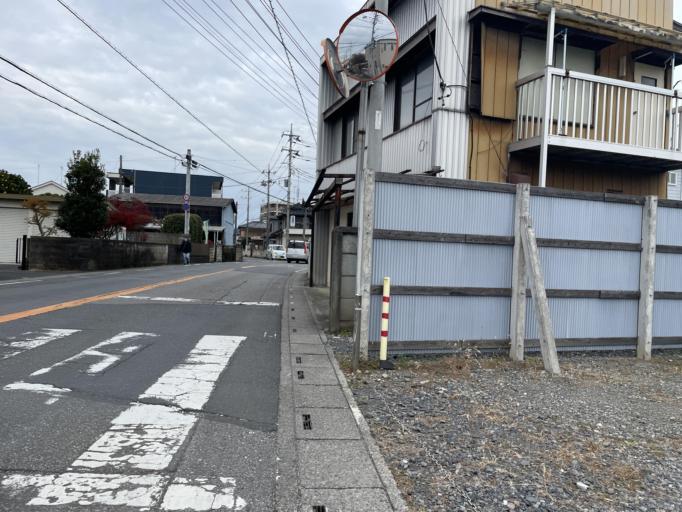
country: JP
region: Saitama
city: Shiraoka
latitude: 36.0119
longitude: 139.6606
